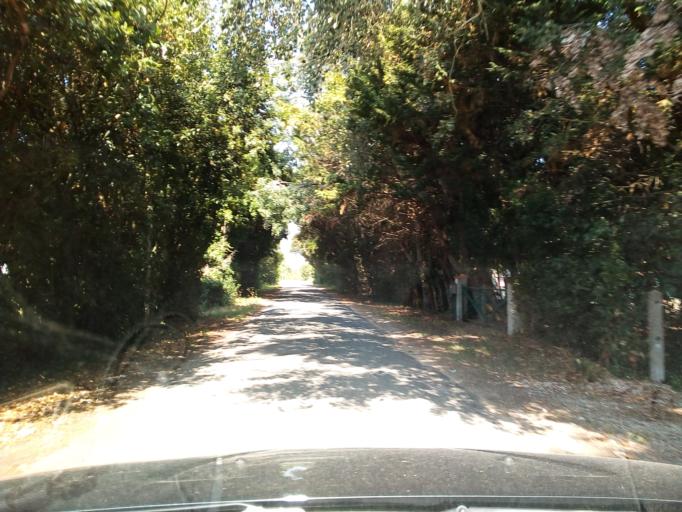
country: FR
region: Poitou-Charentes
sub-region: Departement de la Charente-Maritime
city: Boyard-Ville
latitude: 45.9572
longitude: -1.2596
